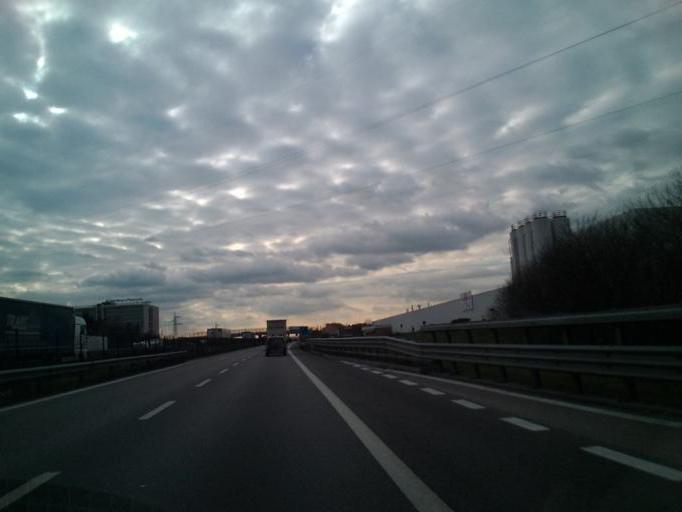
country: IT
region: Veneto
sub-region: Provincia di Verona
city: San Giovanni Lupatoto
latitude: 45.4015
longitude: 11.0233
